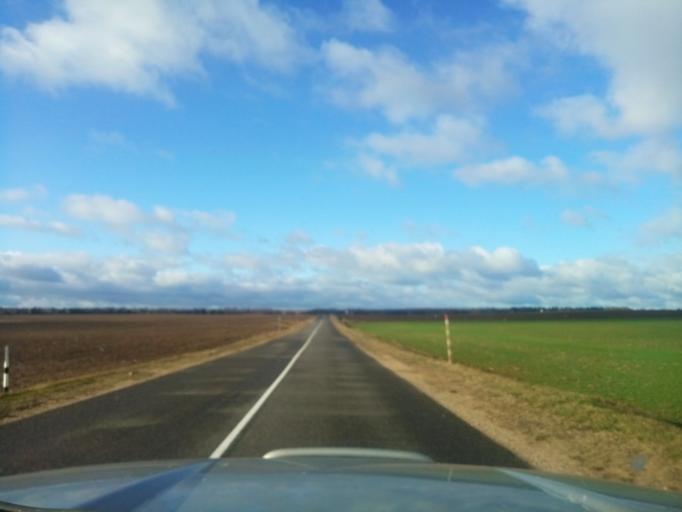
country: BY
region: Minsk
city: Kapyl'
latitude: 53.1692
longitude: 27.0498
